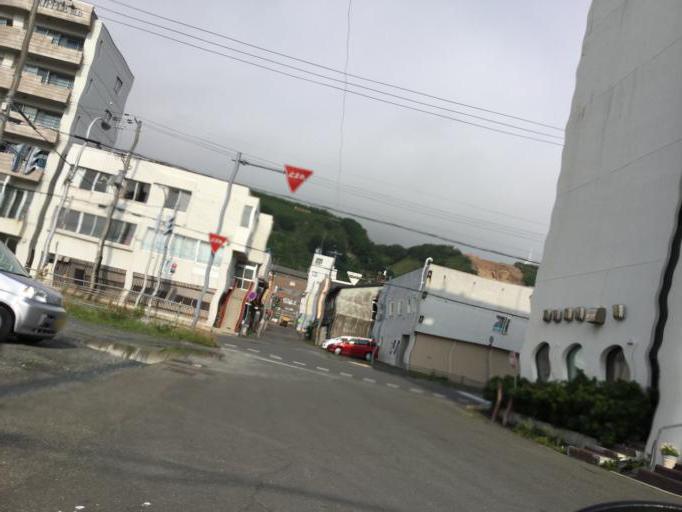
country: JP
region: Hokkaido
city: Wakkanai
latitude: 45.4156
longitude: 141.6767
